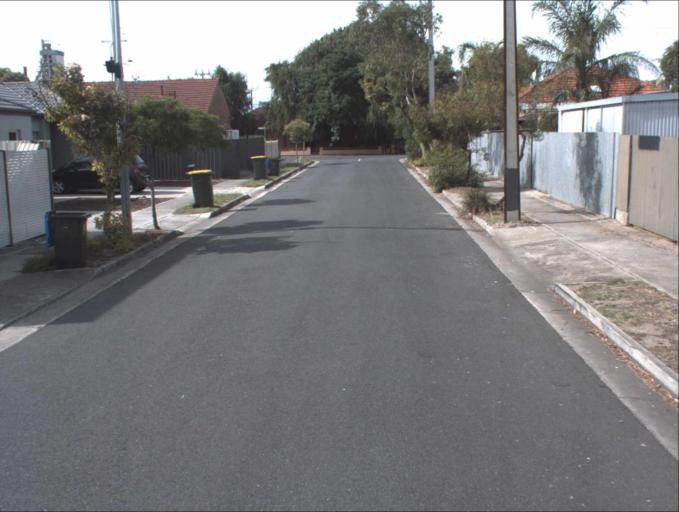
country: AU
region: South Australia
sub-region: Port Adelaide Enfield
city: Birkenhead
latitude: -34.8249
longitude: 138.4977
